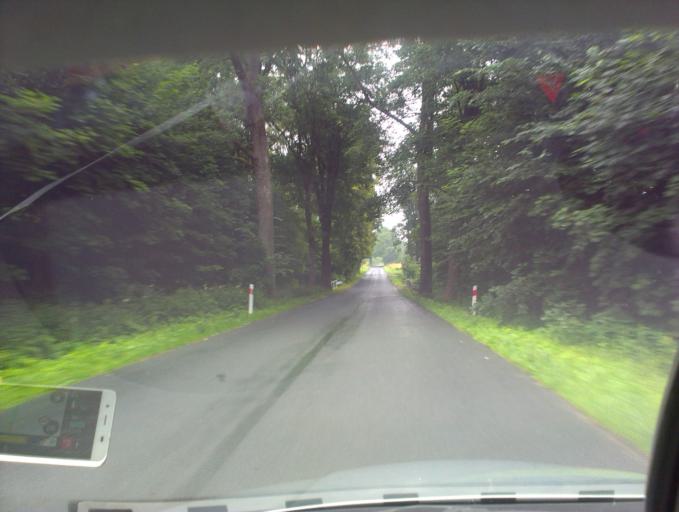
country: PL
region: West Pomeranian Voivodeship
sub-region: Powiat szczecinecki
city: Barwice
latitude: 53.7580
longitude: 16.3678
